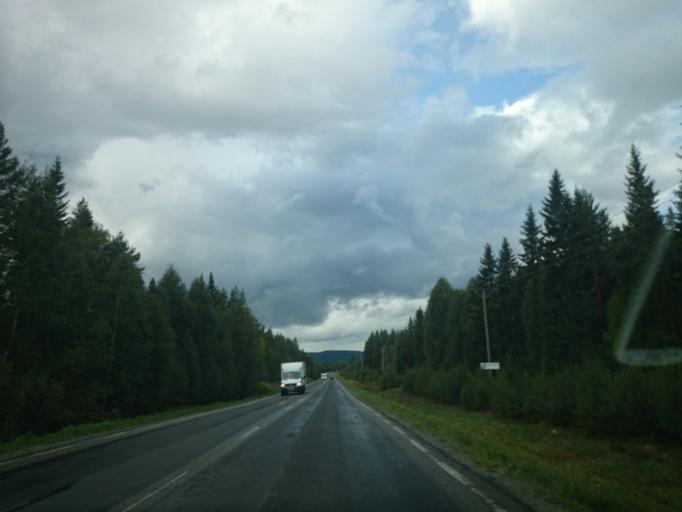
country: SE
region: Vaesternorrland
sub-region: Ange Kommun
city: Ange
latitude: 62.3993
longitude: 15.4587
